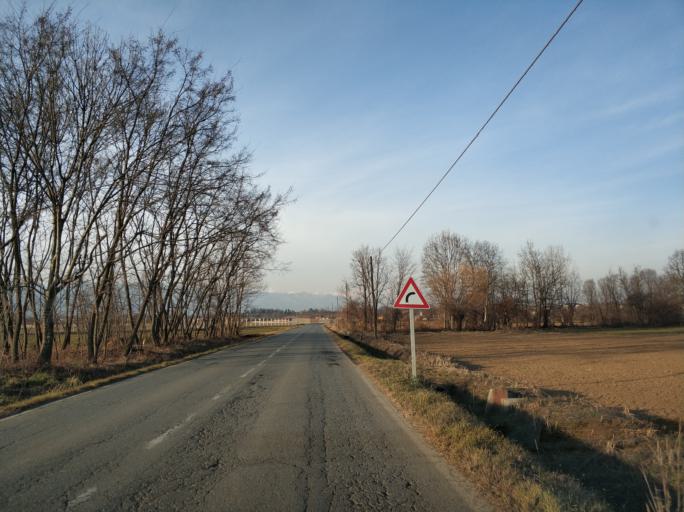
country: IT
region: Piedmont
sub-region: Provincia di Torino
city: San Francesco al Campo
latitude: 45.2149
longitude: 7.6536
